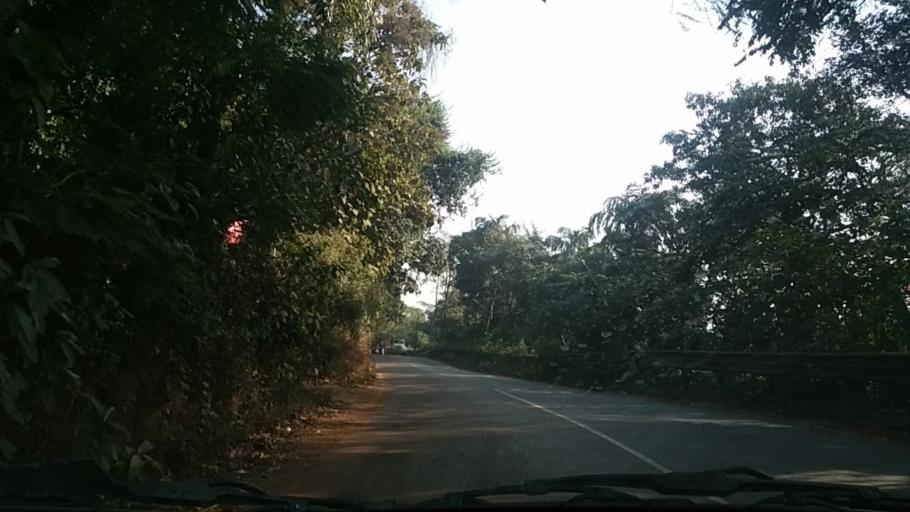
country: IN
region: Goa
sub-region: South Goa
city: Sanvordem
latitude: 15.2689
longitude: 74.1154
